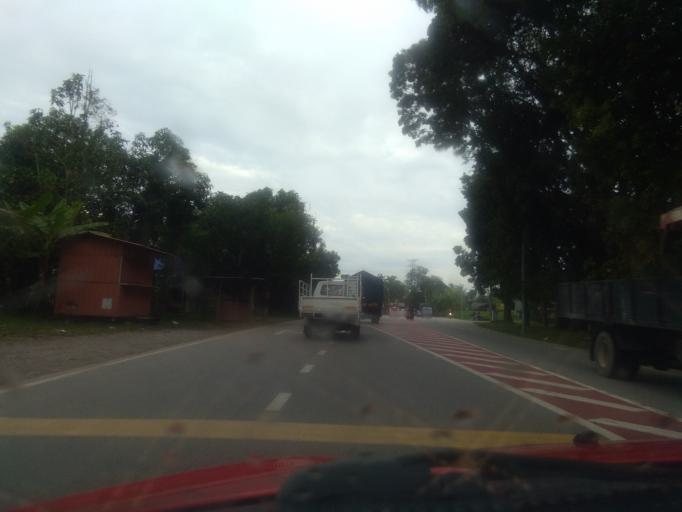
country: MY
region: Kedah
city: Sungai Petani
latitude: 5.6293
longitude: 100.5248
